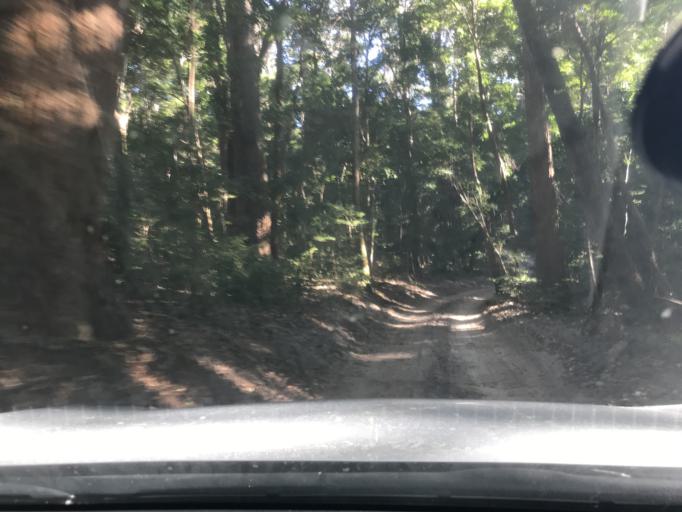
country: AU
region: Queensland
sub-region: Fraser Coast
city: Urangan
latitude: -25.3244
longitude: 153.1523
